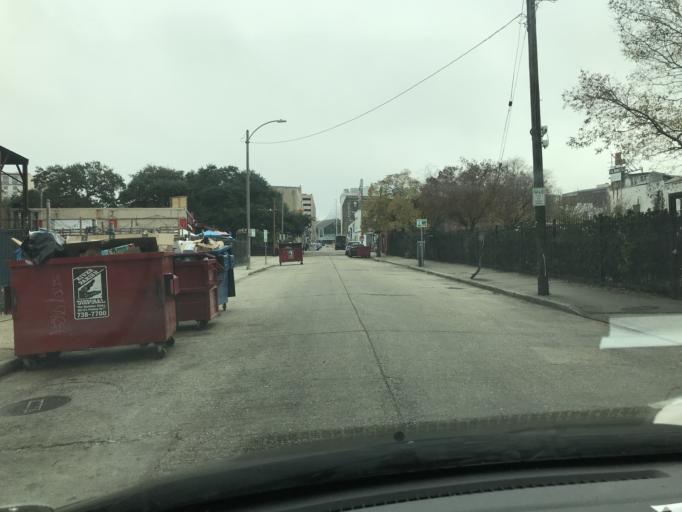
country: US
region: Louisiana
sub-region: Orleans Parish
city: New Orleans
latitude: 29.9424
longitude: -90.0685
